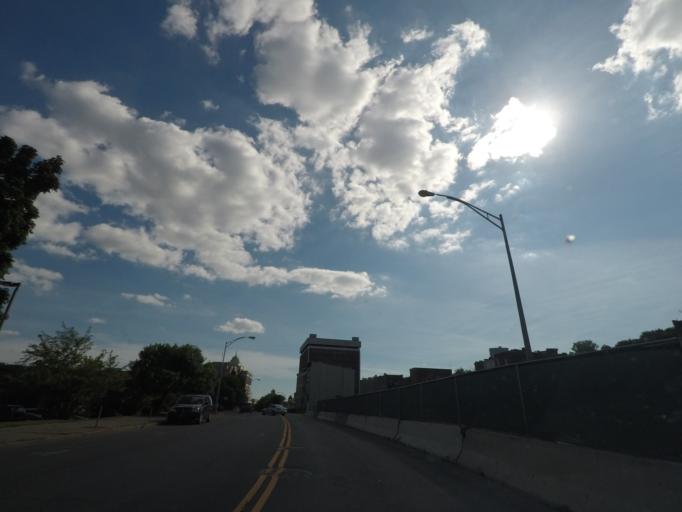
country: US
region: New York
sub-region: Albany County
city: Albany
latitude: 42.6574
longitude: -73.7483
